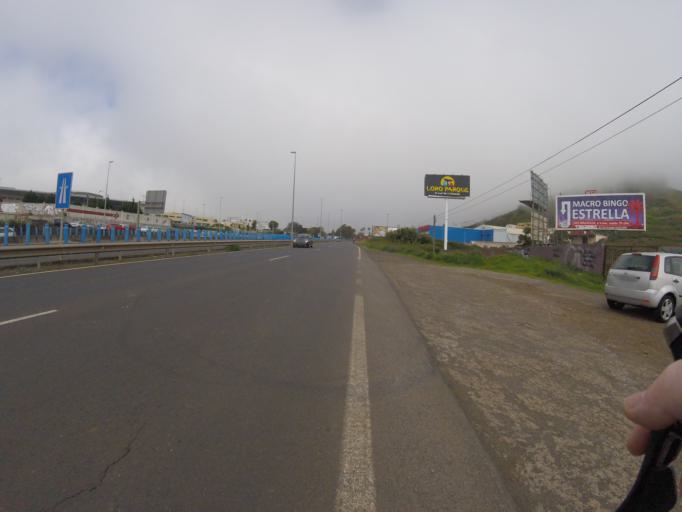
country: ES
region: Canary Islands
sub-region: Provincia de Santa Cruz de Tenerife
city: La Laguna
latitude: 28.4895
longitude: -16.3445
